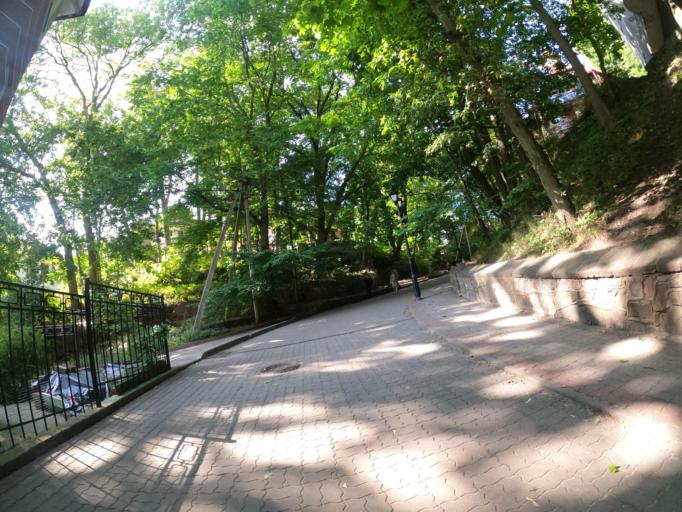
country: RU
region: Kaliningrad
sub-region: Gorod Svetlogorsk
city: Svetlogorsk
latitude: 54.9390
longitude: 20.1567
